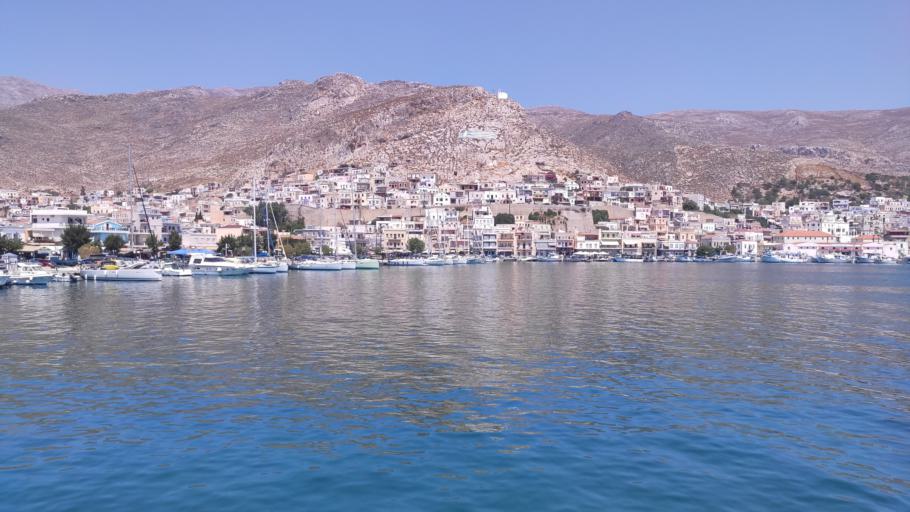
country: GR
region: South Aegean
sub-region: Nomos Dodekanisou
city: Kalymnos
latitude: 36.9490
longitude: 26.9858
